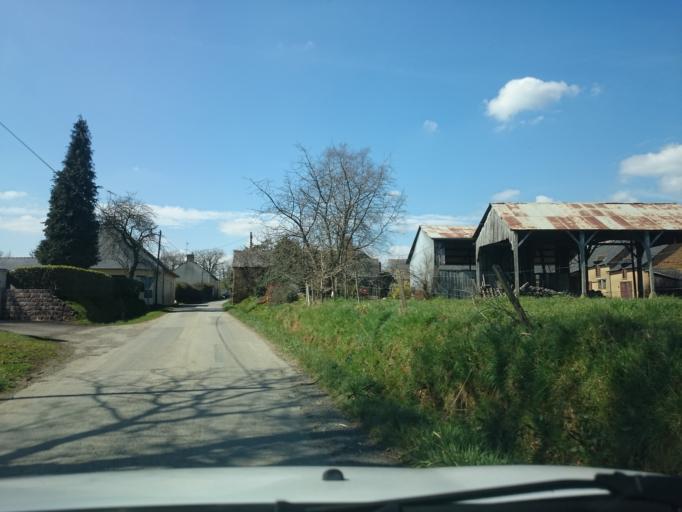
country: FR
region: Brittany
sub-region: Departement d'Ille-et-Vilaine
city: Acigne
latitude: 48.1610
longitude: -1.5169
